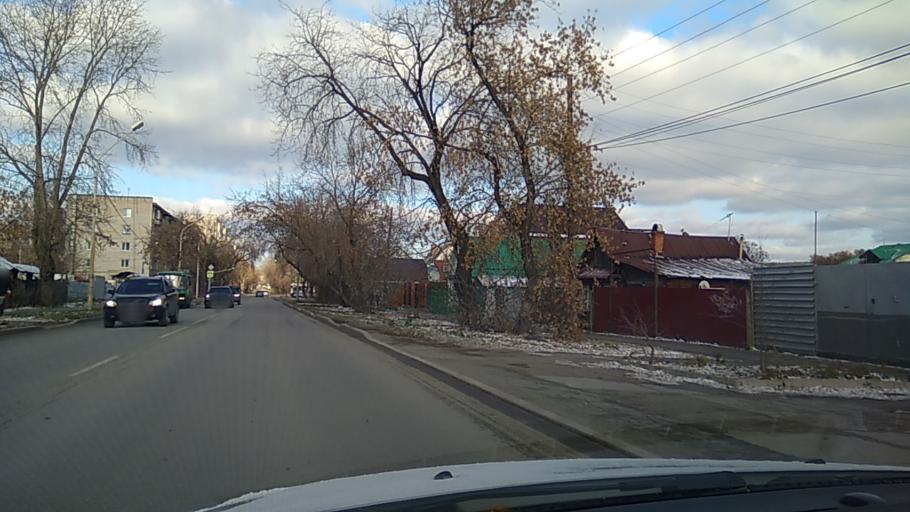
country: RU
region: Sverdlovsk
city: Sovkhoznyy
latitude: 56.7492
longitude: 60.6190
